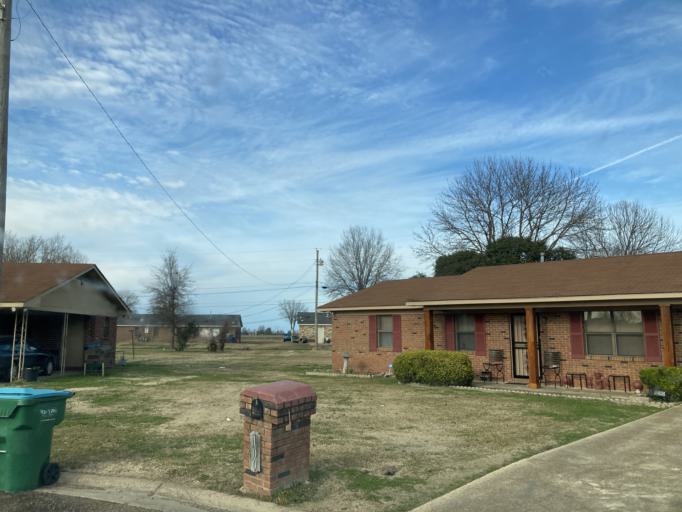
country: US
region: Mississippi
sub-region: Humphreys County
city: Belzoni
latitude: 33.1721
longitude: -90.5018
